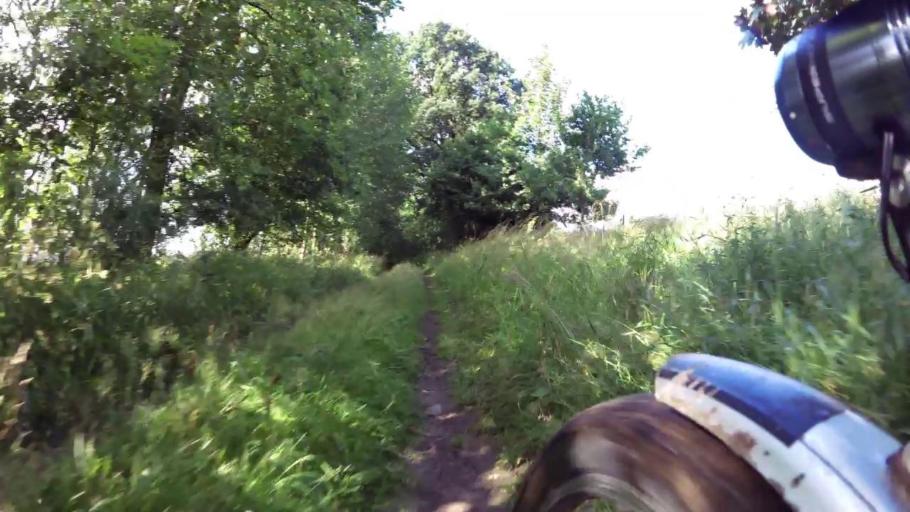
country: PL
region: West Pomeranian Voivodeship
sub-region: Powiat swidwinski
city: Swidwin
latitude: 53.7401
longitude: 15.7564
